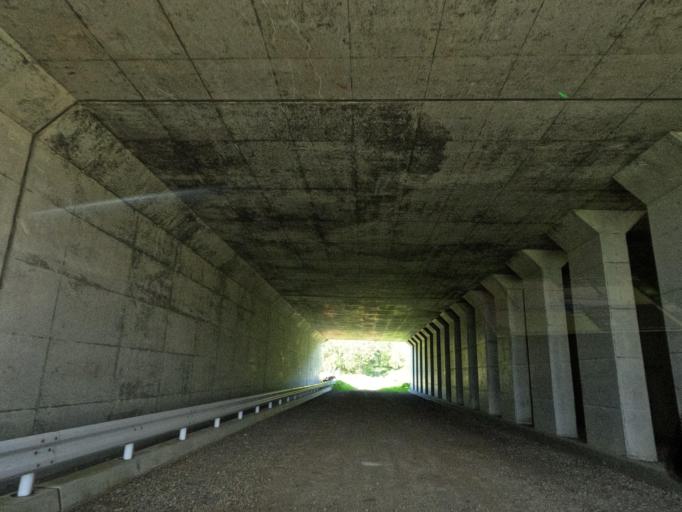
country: JP
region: Hokkaido
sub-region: Asahikawa-shi
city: Asahikawa
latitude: 43.9211
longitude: 142.4955
